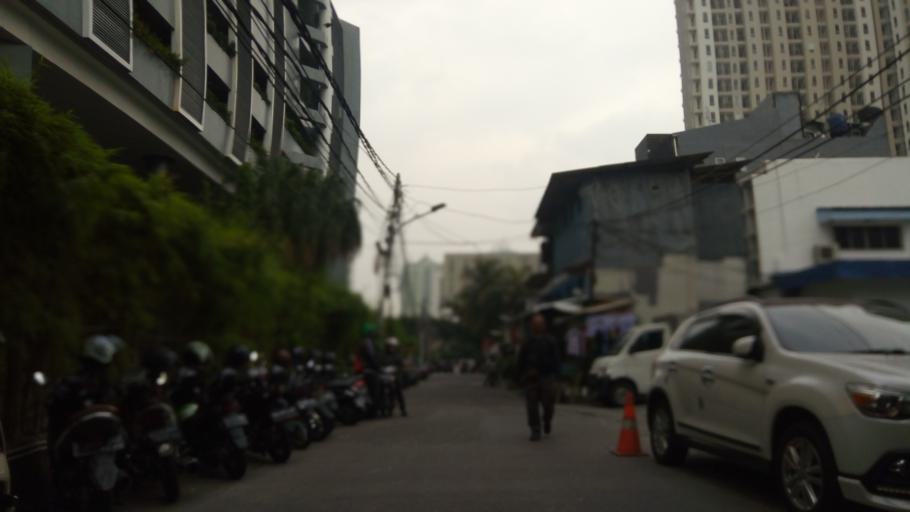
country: ID
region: Jakarta Raya
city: Jakarta
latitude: -6.1493
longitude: 106.8353
